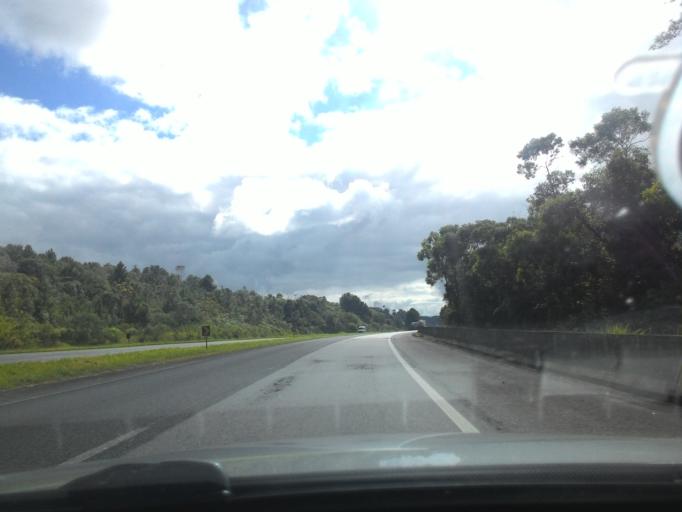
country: BR
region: Sao Paulo
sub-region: Cajati
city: Cajati
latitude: -24.9519
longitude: -48.3179
